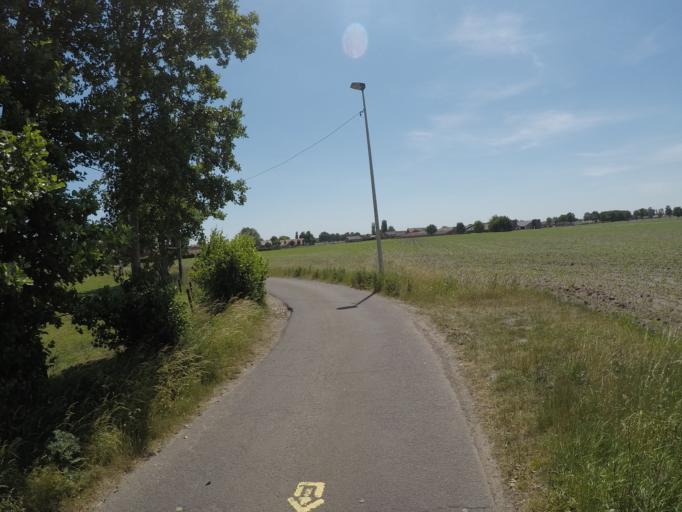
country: BE
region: Flanders
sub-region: Provincie Antwerpen
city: Wuustwezel
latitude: 51.3822
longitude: 4.5584
